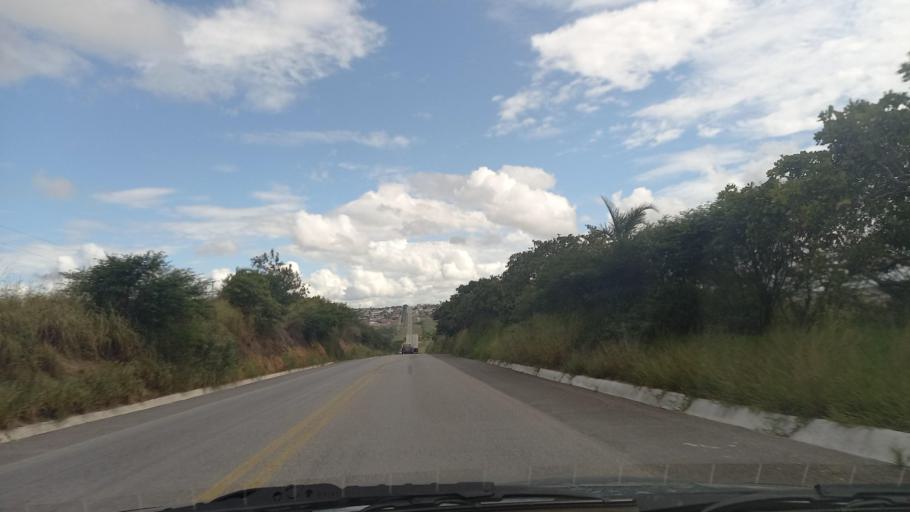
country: BR
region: Pernambuco
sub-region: Lajedo
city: Lajedo
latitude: -8.6886
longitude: -36.4100
